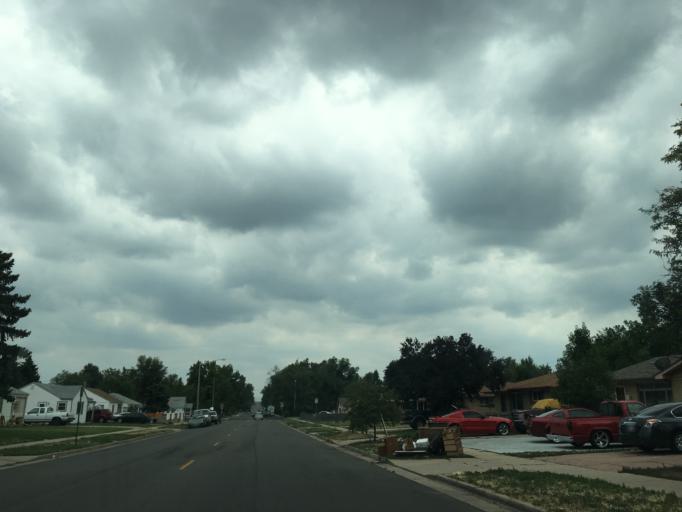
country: US
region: Colorado
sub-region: Arapahoe County
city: Sheridan
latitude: 39.6837
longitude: -105.0159
